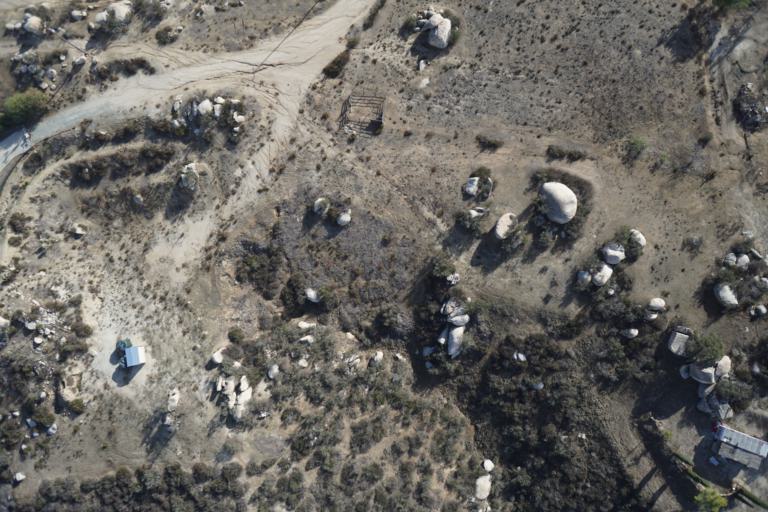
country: US
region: California
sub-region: Riverside County
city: East Hemet
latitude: 33.6424
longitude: -116.9225
